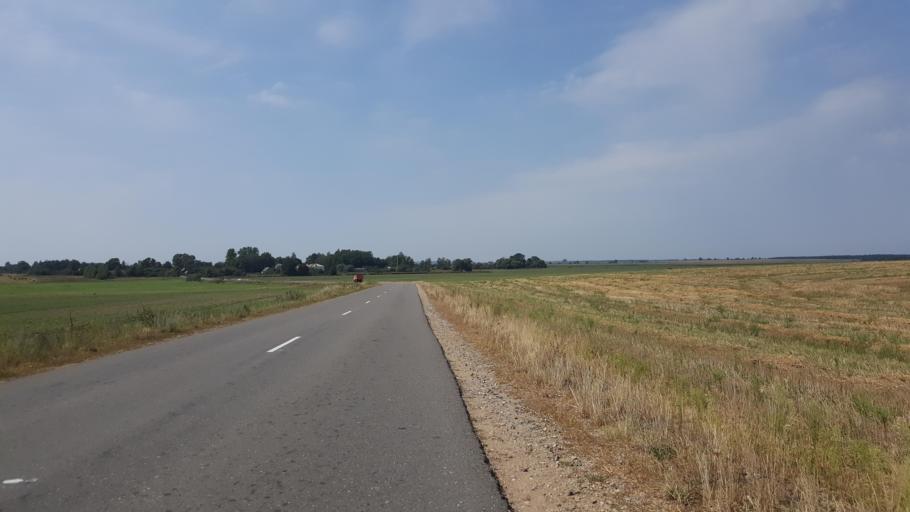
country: BY
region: Brest
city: Kamyanyets
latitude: 52.4728
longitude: 23.7029
